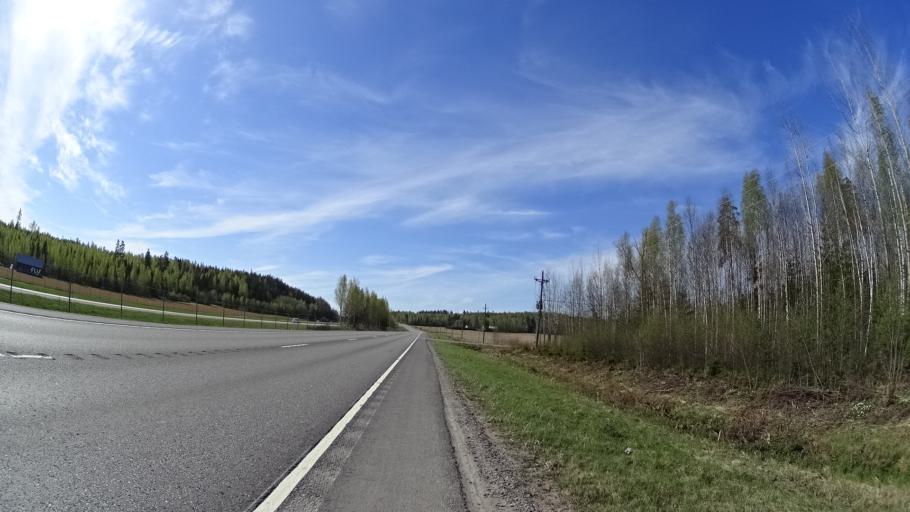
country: FI
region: Uusimaa
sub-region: Helsinki
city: Nurmijaervi
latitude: 60.4259
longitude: 24.8254
